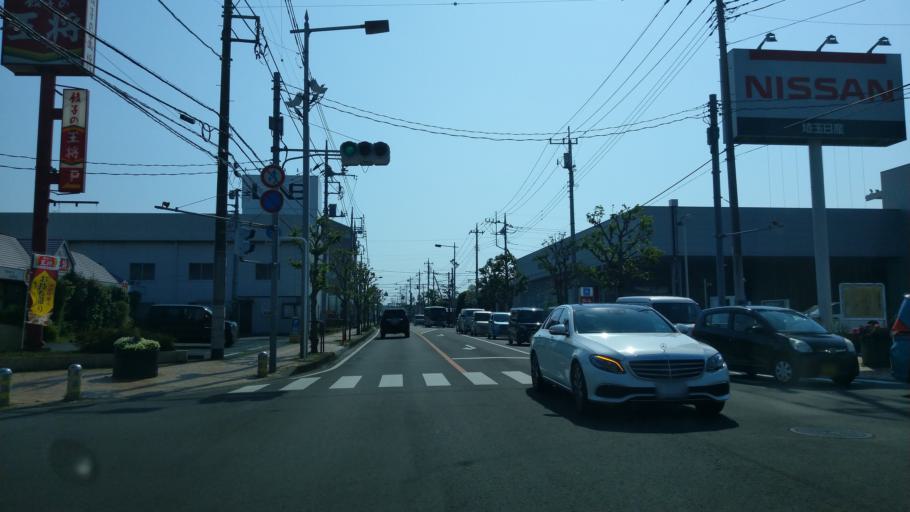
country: JP
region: Saitama
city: Oi
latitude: 35.8550
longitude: 139.5185
